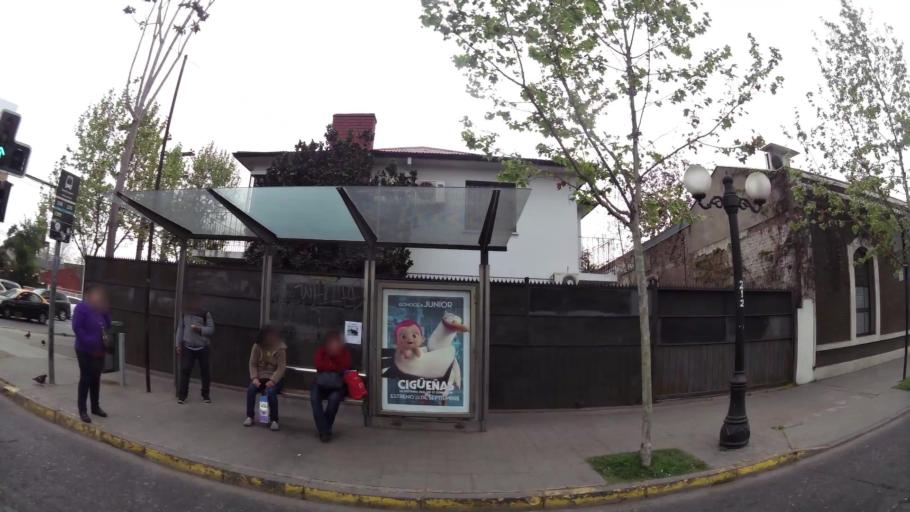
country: CL
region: Santiago Metropolitan
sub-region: Provincia de Santiago
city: Santiago
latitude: -33.4466
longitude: -70.6140
